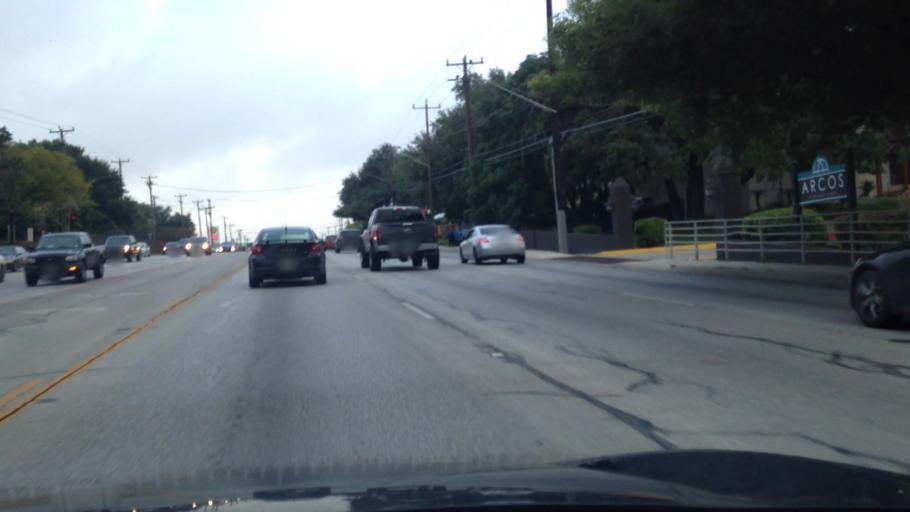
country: US
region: Texas
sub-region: Bexar County
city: Balcones Heights
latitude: 29.5085
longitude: -98.5651
